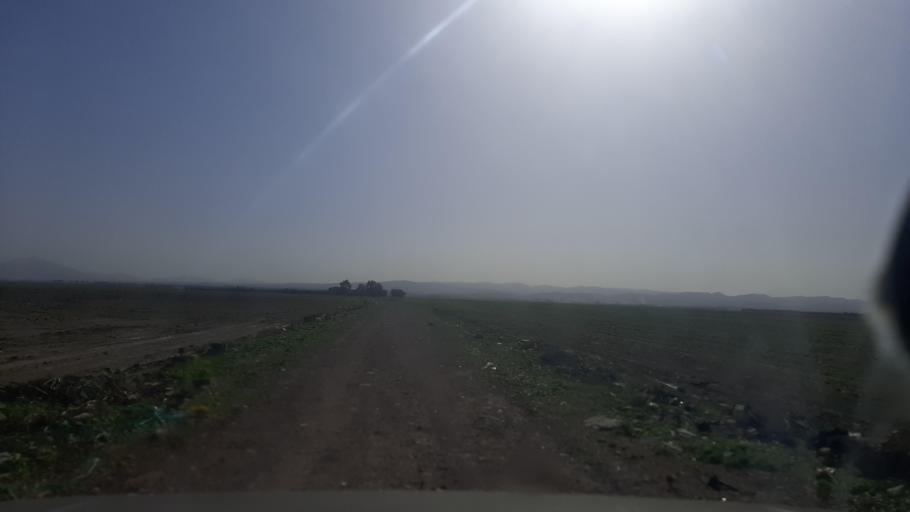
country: TN
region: Tunis
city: La Mohammedia
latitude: 36.6466
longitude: 10.0873
